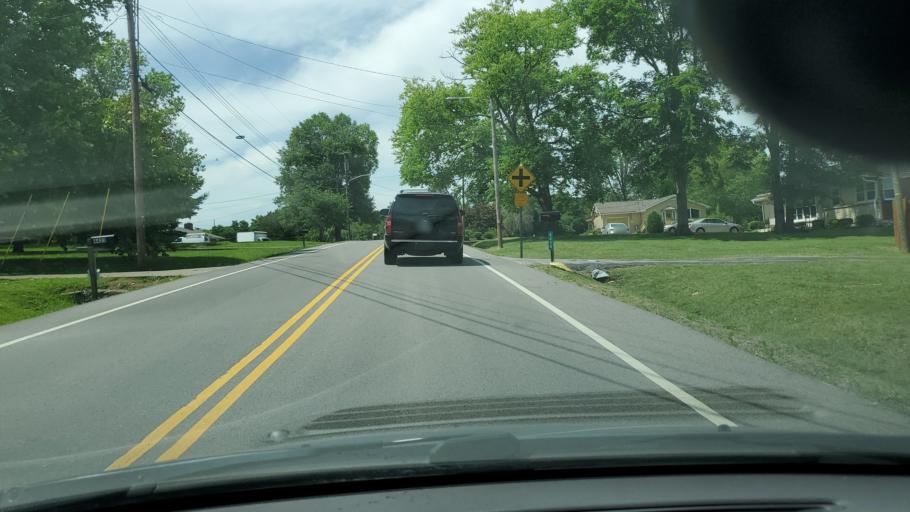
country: US
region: Tennessee
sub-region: Davidson County
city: Nashville
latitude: 36.2334
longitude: -86.7319
